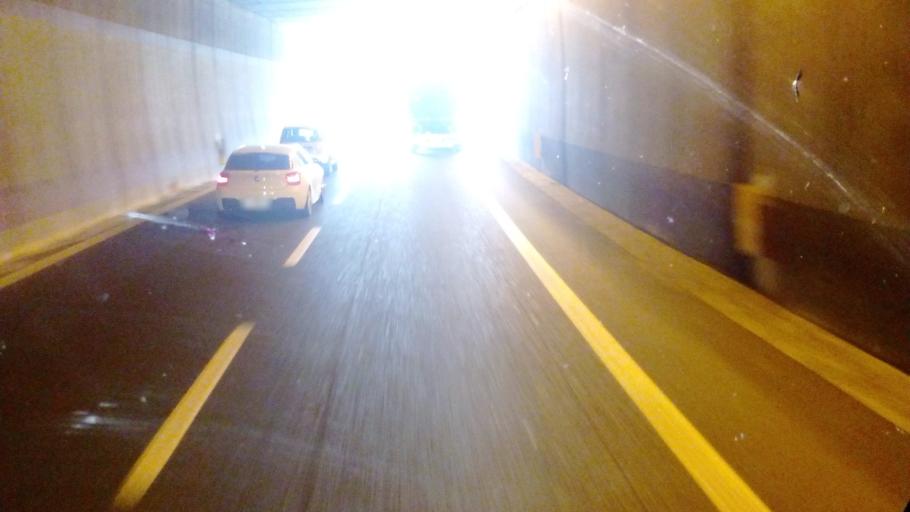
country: IT
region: Lombardy
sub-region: Provincia di Monza e Brianza
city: Lentate sul Seveso
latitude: 45.6812
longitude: 9.1069
